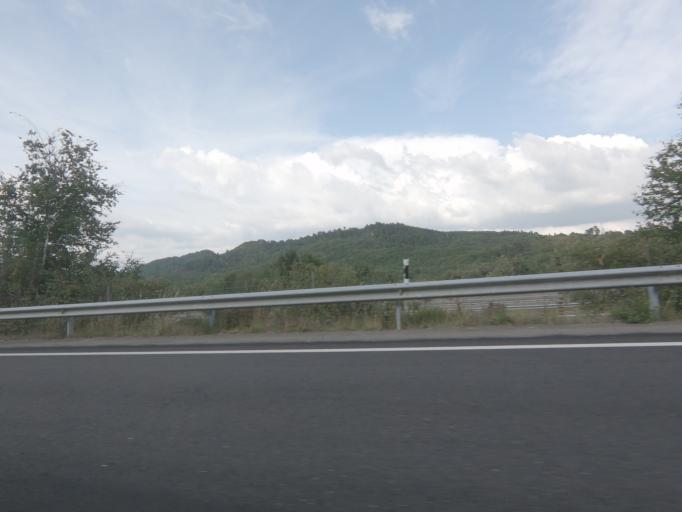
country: ES
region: Galicia
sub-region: Provincia de Ourense
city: Ambia
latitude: 42.1695
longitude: -7.7616
